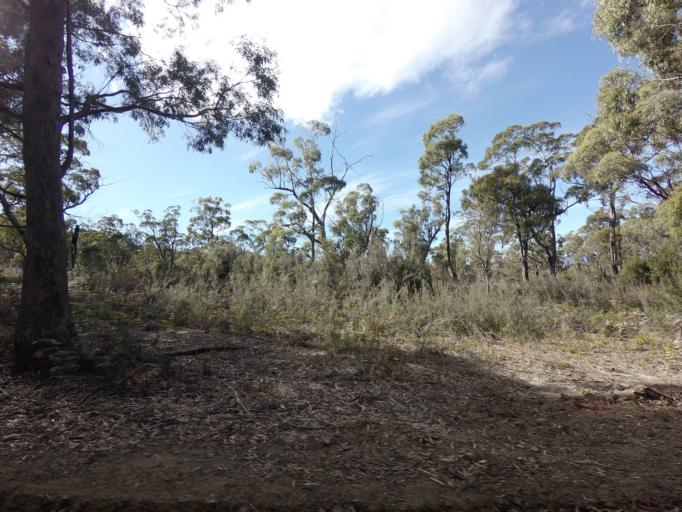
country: AU
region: Tasmania
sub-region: Clarence
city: Sandford
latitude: -42.9724
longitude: 147.7164
